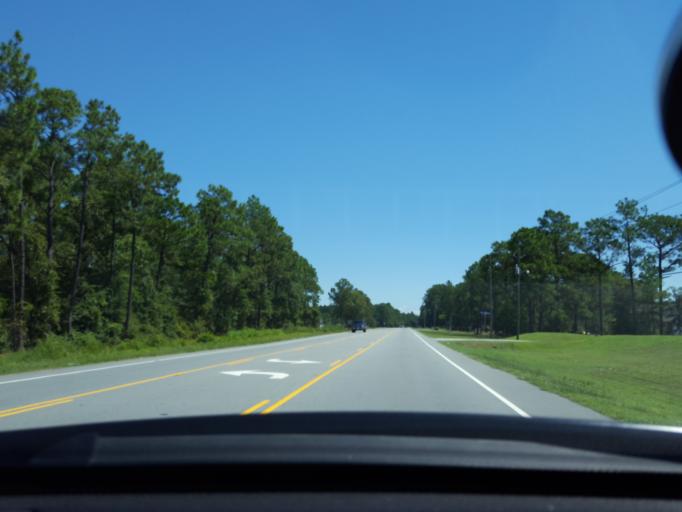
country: US
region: North Carolina
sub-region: Bladen County
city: Elizabethtown
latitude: 34.6480
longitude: -78.5503
